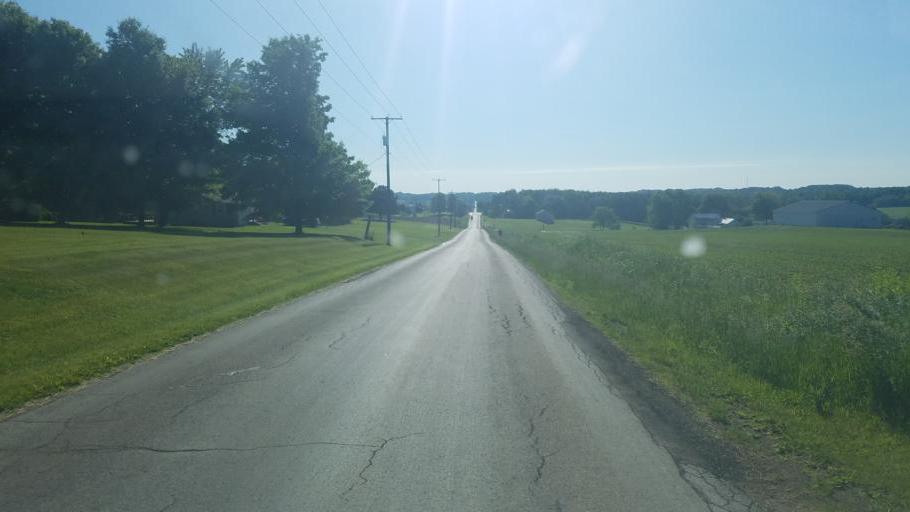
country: US
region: Ohio
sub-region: Richland County
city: Lexington
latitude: 40.5864
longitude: -82.6032
